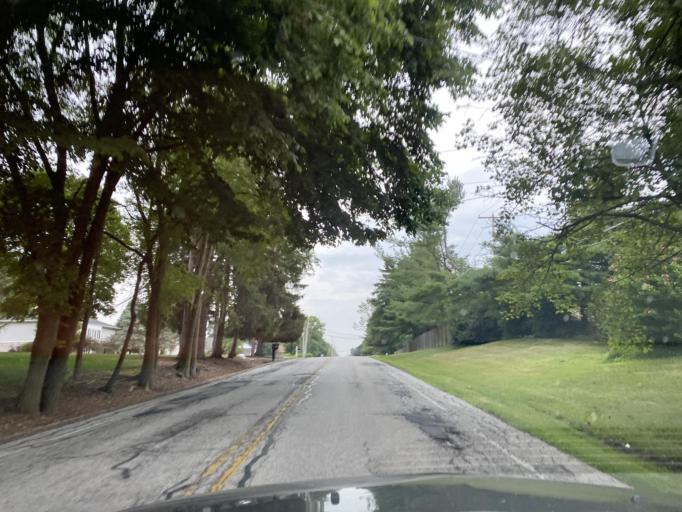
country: US
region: Ohio
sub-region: Summit County
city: Fairlawn
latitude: 41.1442
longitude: -81.5873
